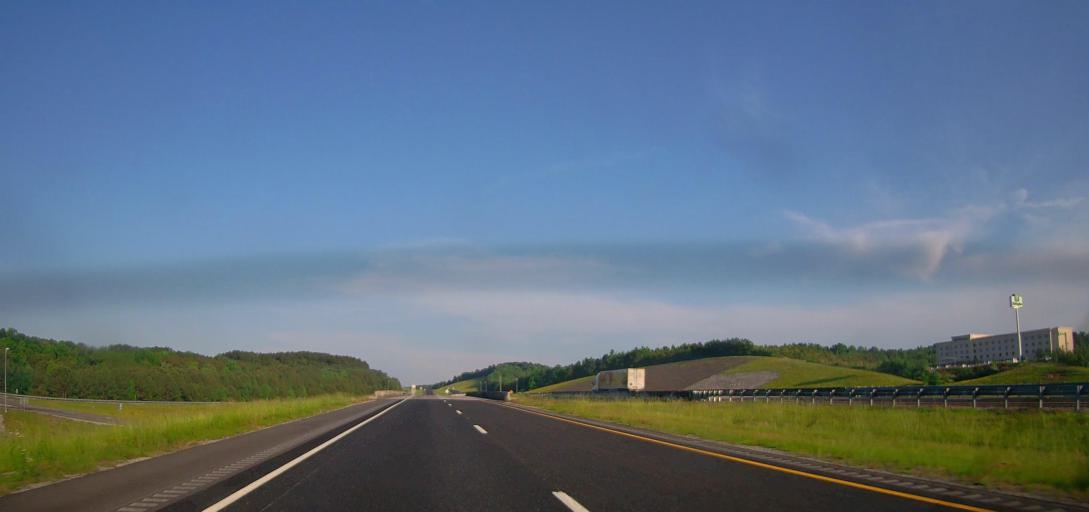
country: US
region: Alabama
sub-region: Marion County
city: Winfield
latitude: 34.0129
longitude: -87.8350
